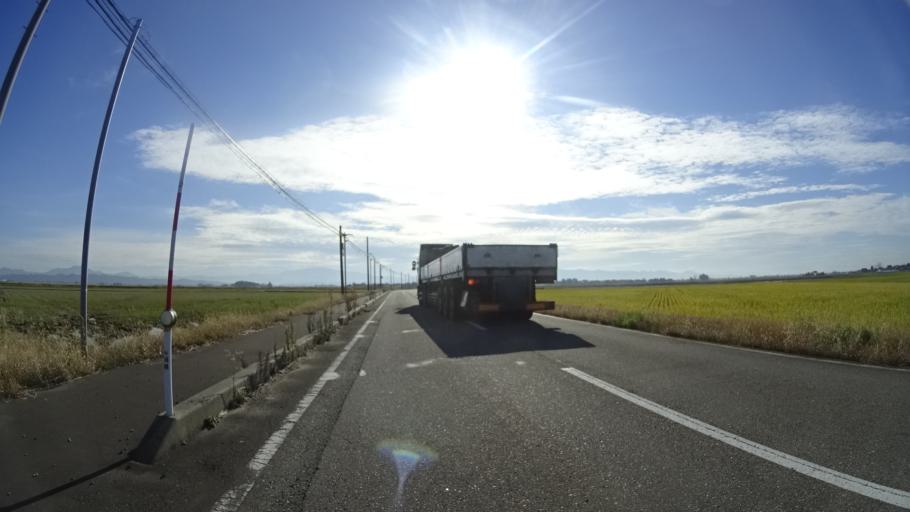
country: JP
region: Niigata
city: Mitsuke
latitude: 37.5680
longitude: 138.8443
